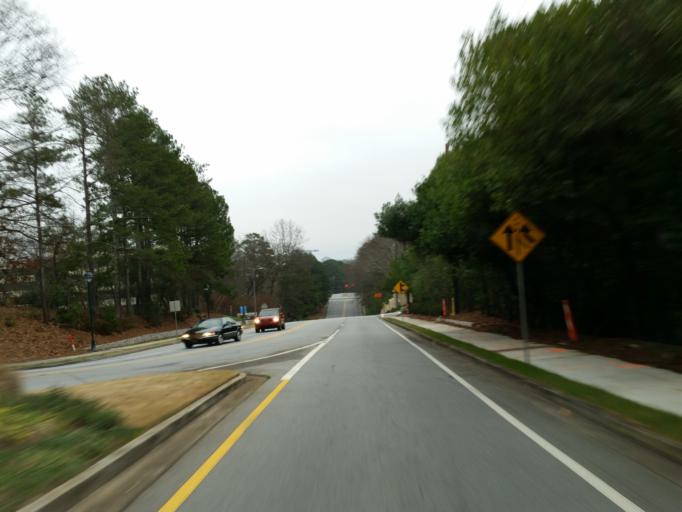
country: US
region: Georgia
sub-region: Fulton County
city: Sandy Springs
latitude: 33.9193
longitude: -84.3911
